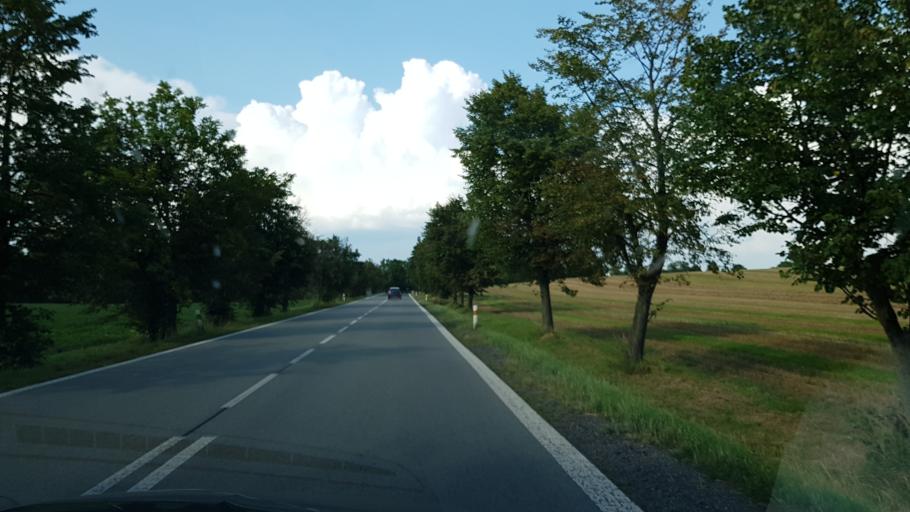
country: CZ
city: Vamberk
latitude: 50.1088
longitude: 16.3791
